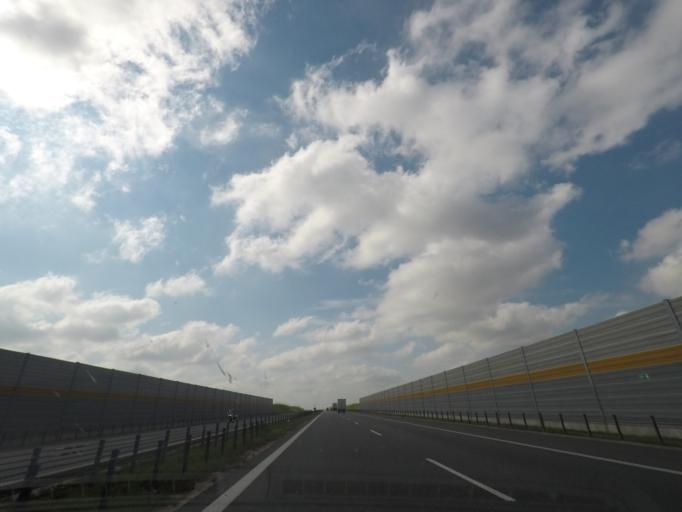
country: PL
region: Kujawsko-Pomorskie
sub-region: Powiat chelminski
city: Lisewo
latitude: 53.2447
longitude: 18.7251
